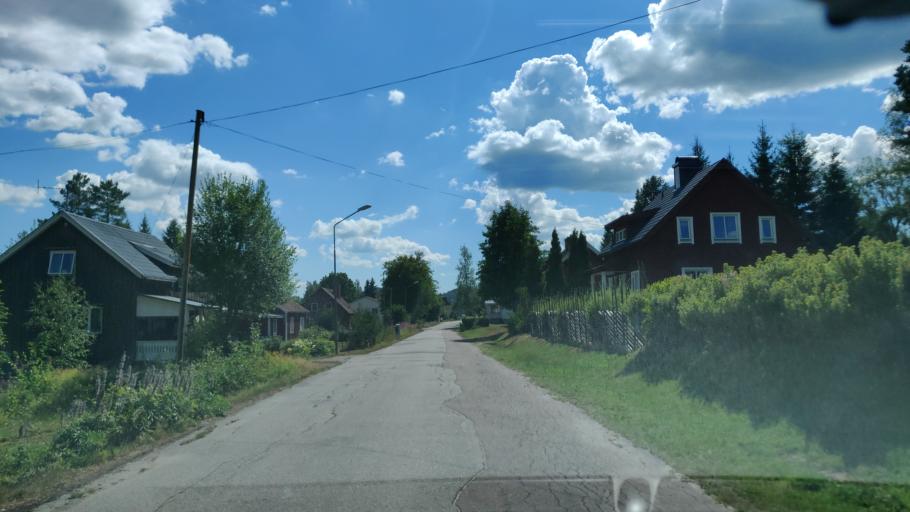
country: SE
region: Vaermland
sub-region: Hagfors Kommun
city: Ekshaerad
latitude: 60.1783
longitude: 13.4938
